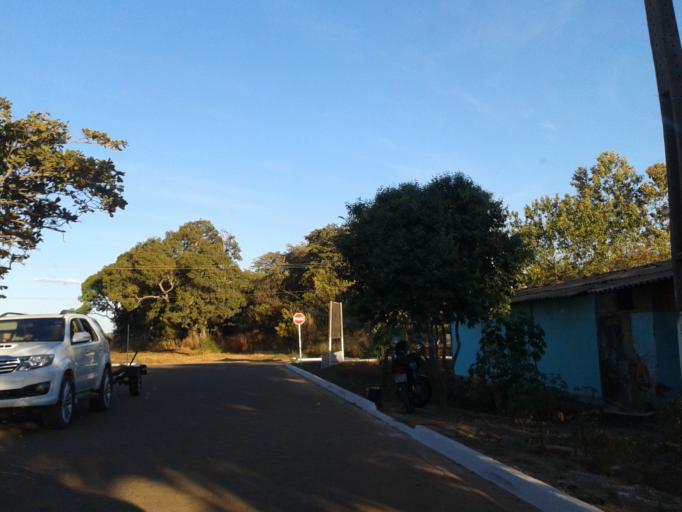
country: BR
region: Goias
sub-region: Sao Miguel Do Araguaia
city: Sao Miguel do Araguaia
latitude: -13.2183
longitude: -50.5750
